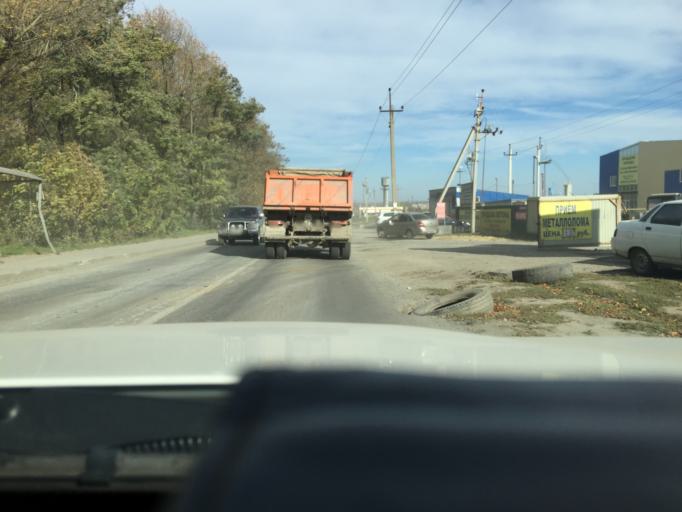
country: RU
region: Rostov
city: Imeni Chkalova
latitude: 47.2952
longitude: 39.8036
